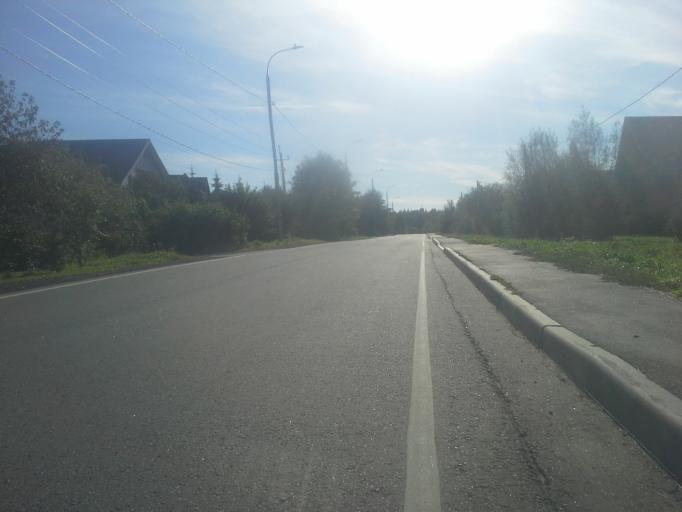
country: RU
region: Moskovskaya
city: Selyatino
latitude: 55.4097
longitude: 37.0103
